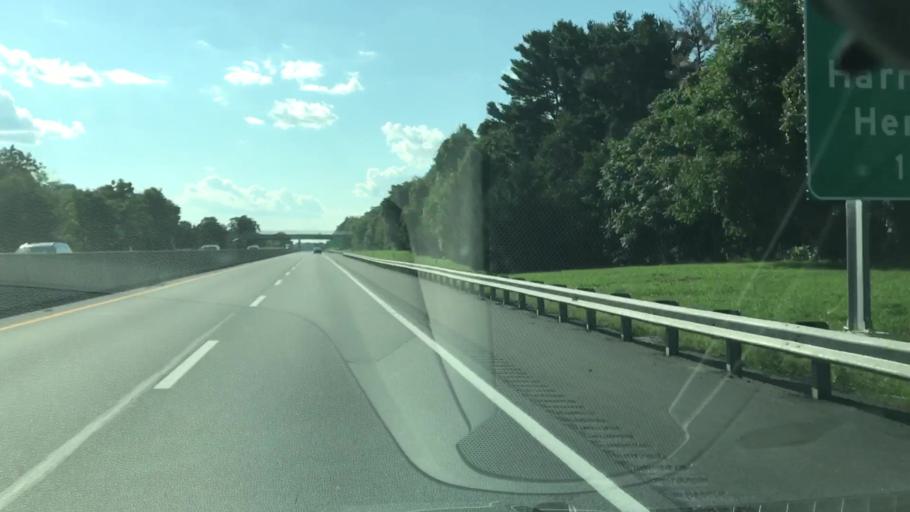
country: US
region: Pennsylvania
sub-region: Dauphin County
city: Highspire
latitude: 40.2129
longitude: -76.7672
